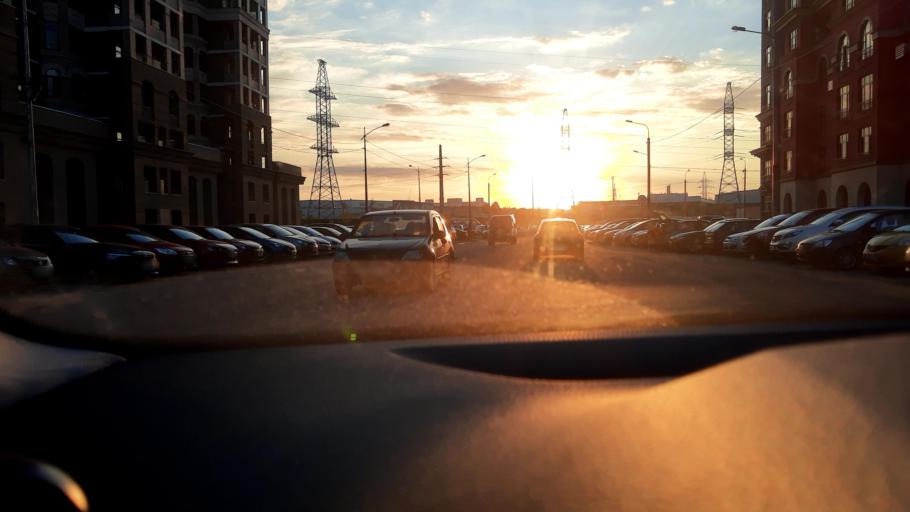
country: RU
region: Moscow
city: Khimki
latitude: 55.9170
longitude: 37.4087
